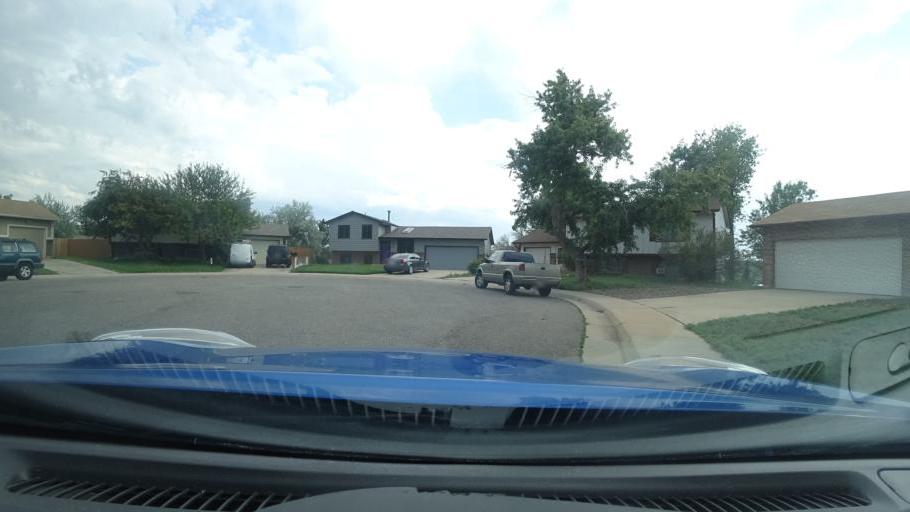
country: US
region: Colorado
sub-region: Adams County
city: Aurora
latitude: 39.6864
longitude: -104.7973
